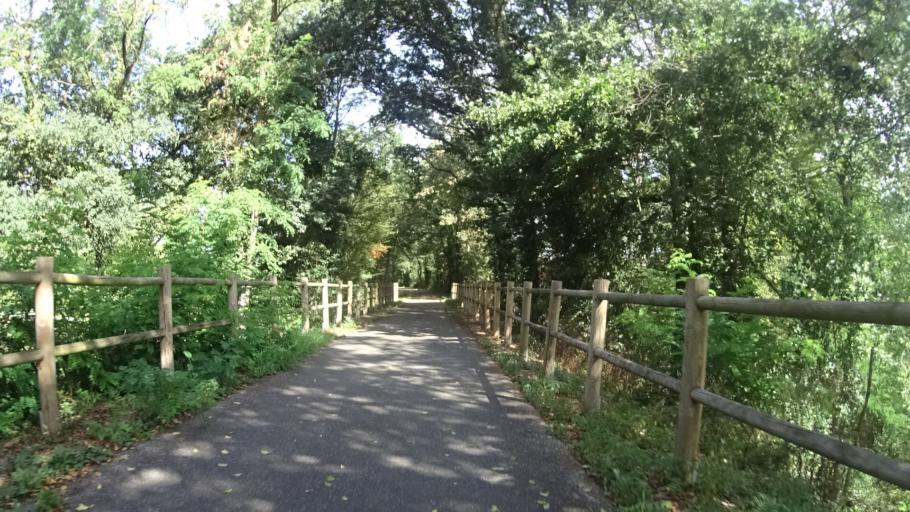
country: FR
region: Bourgogne
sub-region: Departement de Saone-et-Loire
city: Bourbon-Lancy
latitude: 46.6189
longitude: 3.7405
